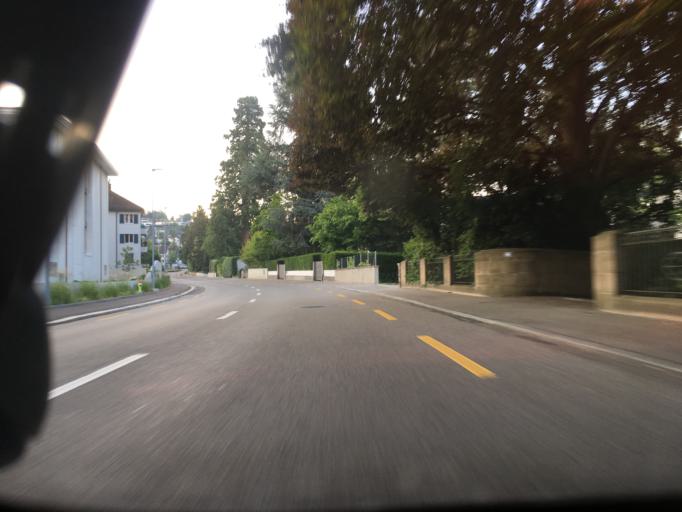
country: CH
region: Zurich
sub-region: Bezirk Meilen
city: Erlenbach
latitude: 47.3006
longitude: 8.5934
